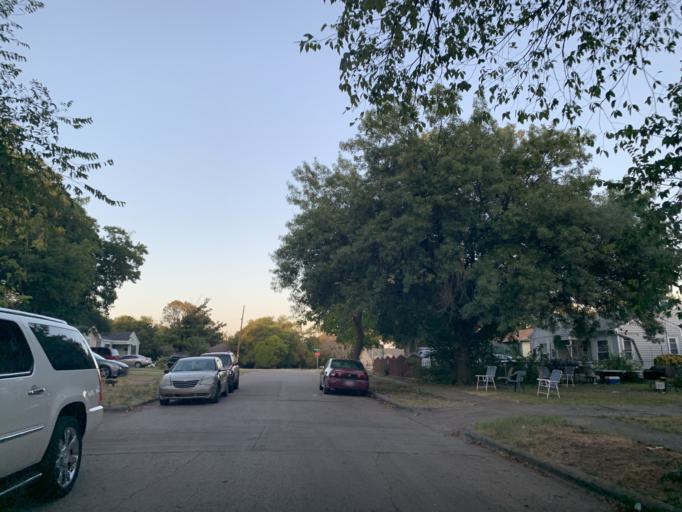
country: US
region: Texas
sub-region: Dallas County
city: Dallas
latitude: 32.6945
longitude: -96.8061
